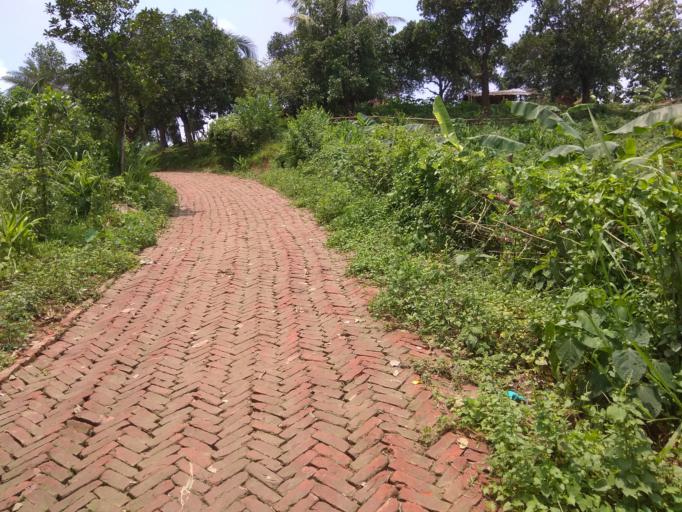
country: BD
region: Chittagong
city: Manikchari
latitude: 22.8844
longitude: 91.9261
